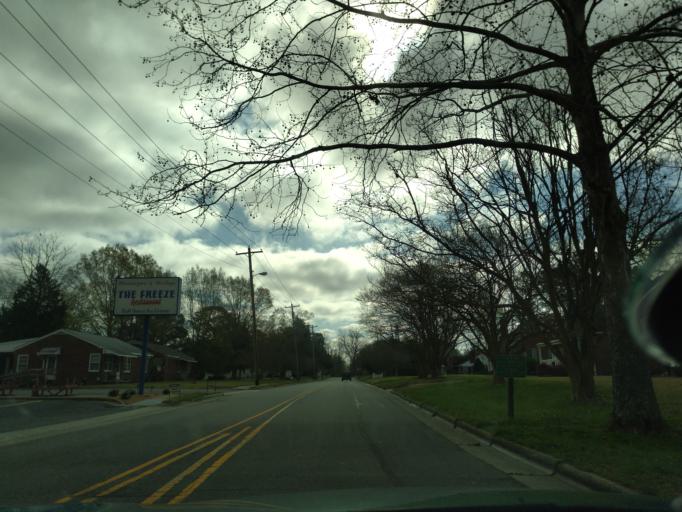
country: US
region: North Carolina
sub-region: Chowan County
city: Edenton
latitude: 36.0614
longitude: -76.6161
